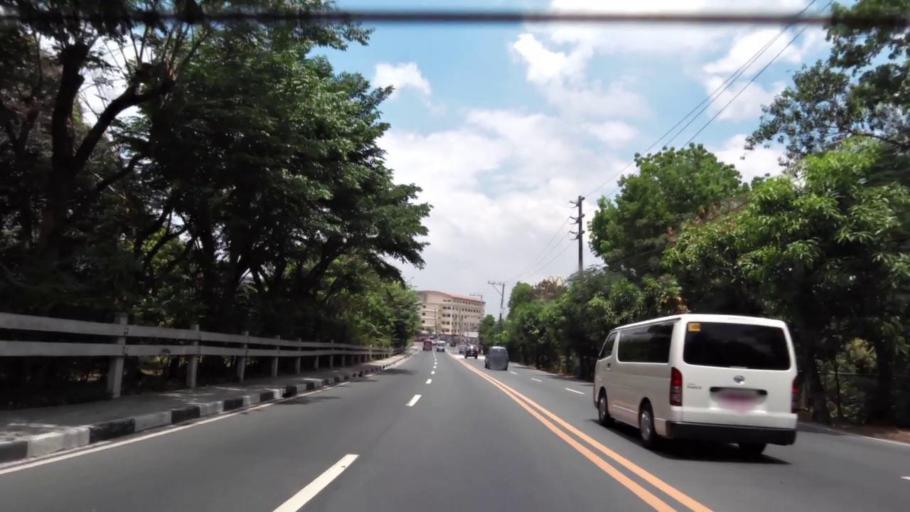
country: PH
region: Calabarzon
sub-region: Province of Rizal
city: Antipolo
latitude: 14.6170
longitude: 121.1527
